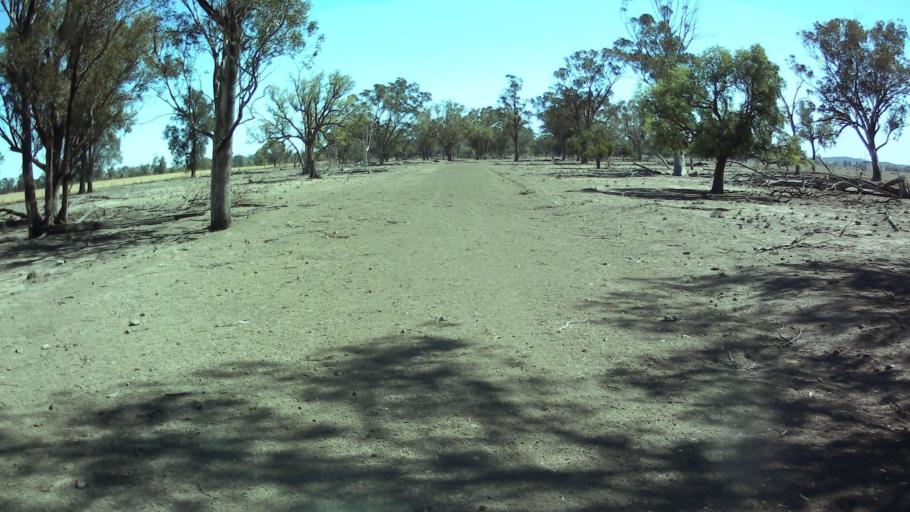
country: AU
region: New South Wales
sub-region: Bland
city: West Wyalong
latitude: -33.7672
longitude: 147.6573
